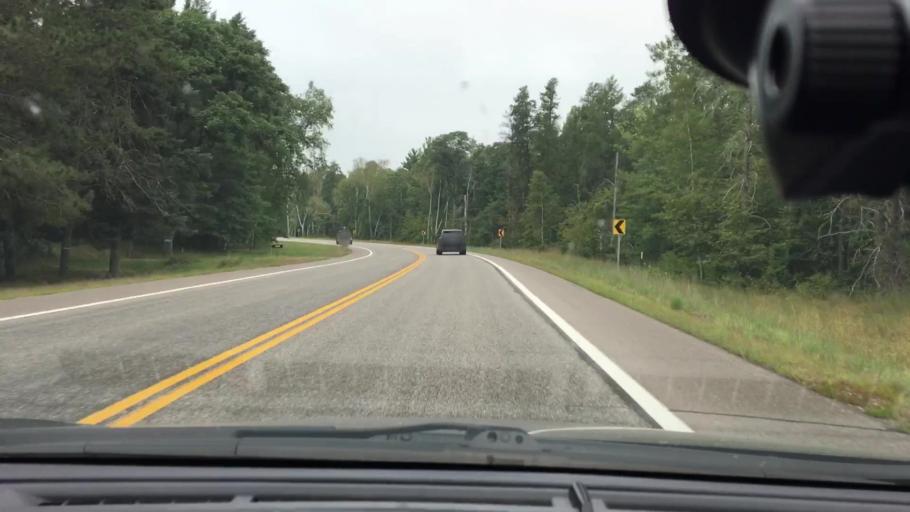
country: US
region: Minnesota
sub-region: Crow Wing County
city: Cross Lake
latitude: 46.6650
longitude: -94.0387
